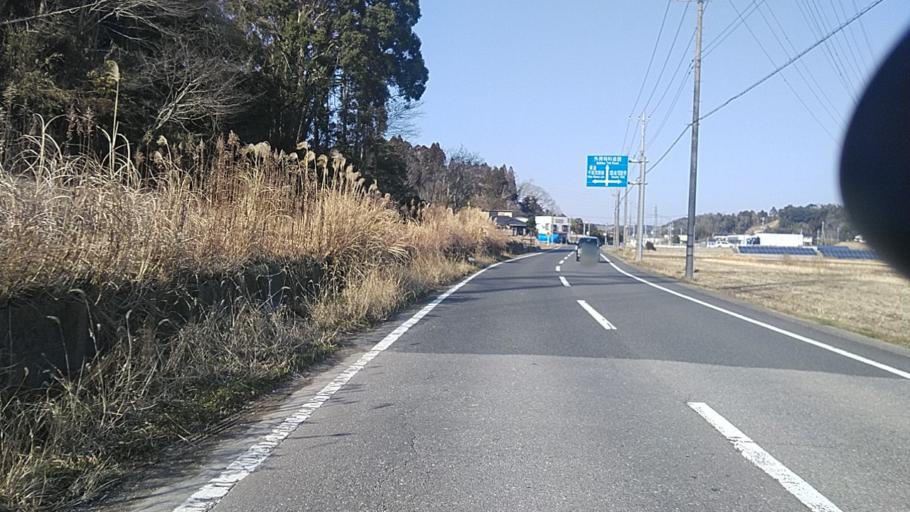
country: JP
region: Chiba
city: Mobara
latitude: 35.4660
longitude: 140.2825
